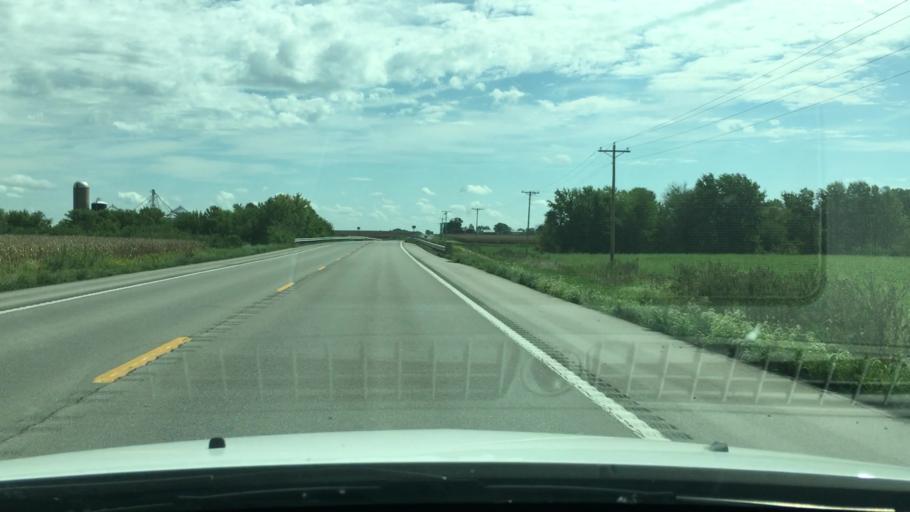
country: US
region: Missouri
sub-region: Montgomery County
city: Wellsville
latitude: 39.1645
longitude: -91.7068
